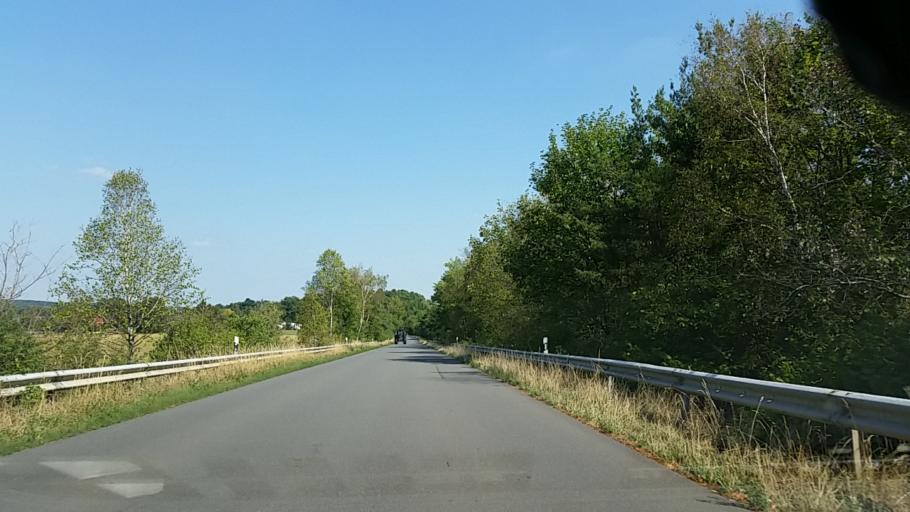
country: DE
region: Lower Saxony
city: Emmendorf
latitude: 53.0133
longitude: 10.5703
